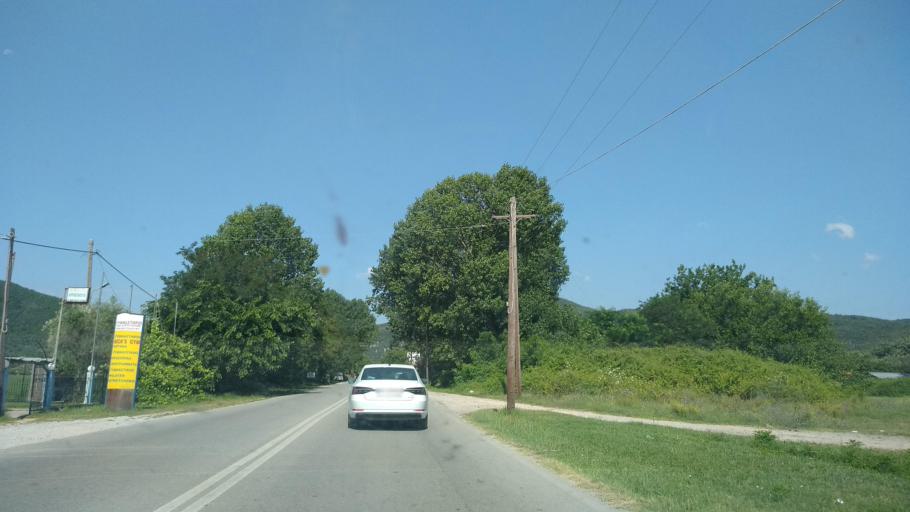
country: GR
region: Central Macedonia
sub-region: Nomos Thessalonikis
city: Stavros
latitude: 40.6680
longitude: 23.6814
